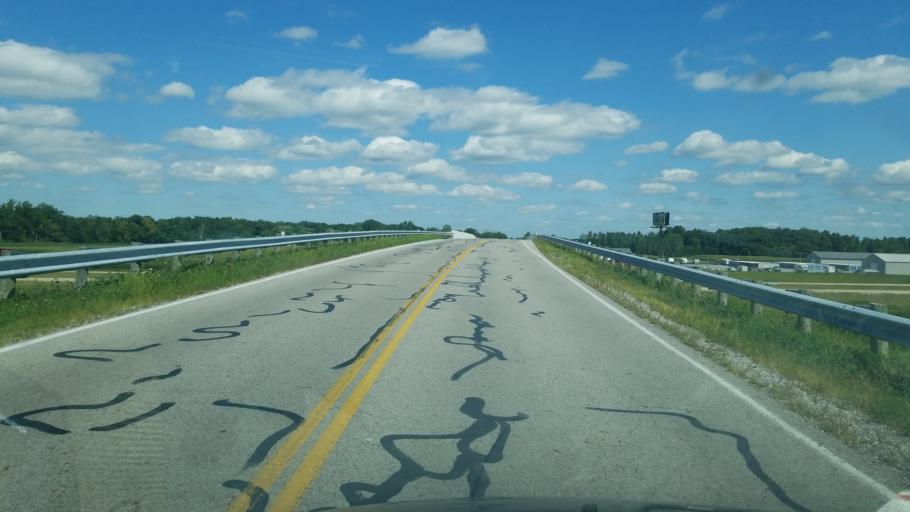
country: US
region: Ohio
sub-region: Lucas County
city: Whitehouse
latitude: 41.4329
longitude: -83.8730
